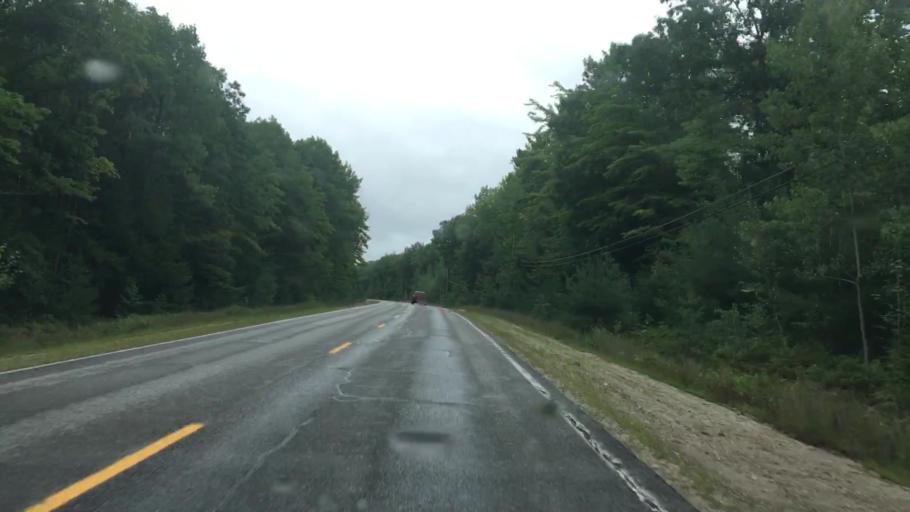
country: US
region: Maine
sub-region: Oxford County
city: Brownfield
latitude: 43.9733
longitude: -70.9228
